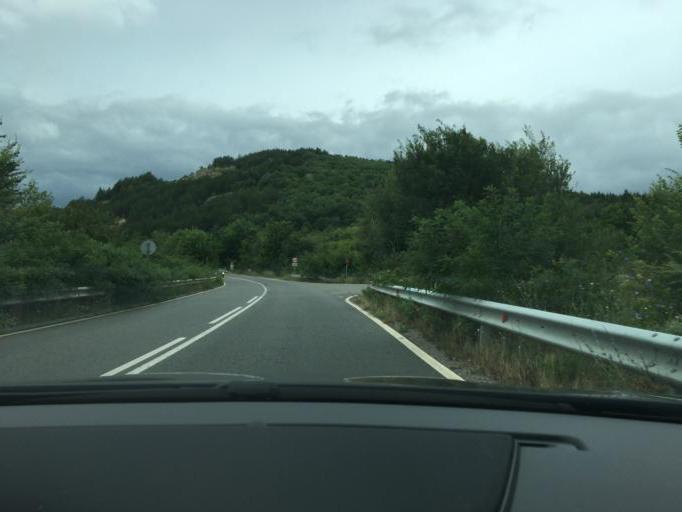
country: BG
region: Kyustendil
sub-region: Obshtina Bobovdol
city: Bobovdol
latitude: 42.2728
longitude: 22.9687
